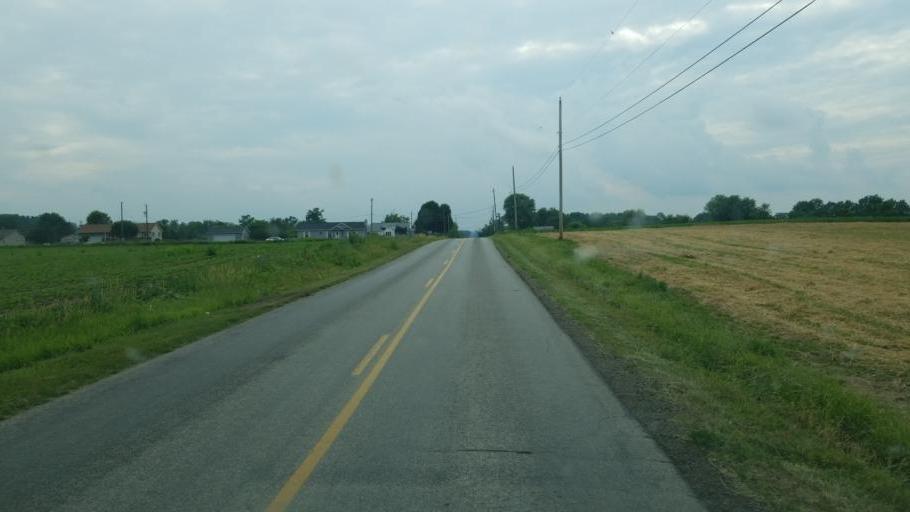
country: US
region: Ohio
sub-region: Wayne County
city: Wooster
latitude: 40.7846
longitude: -81.9047
